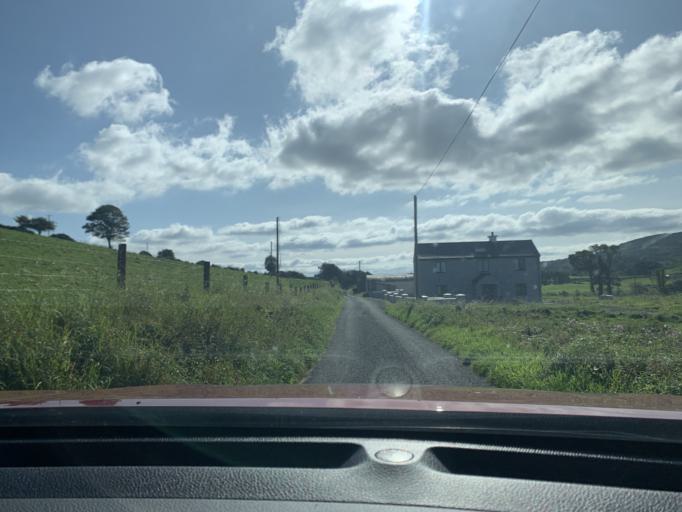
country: IE
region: Connaught
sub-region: Roscommon
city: Boyle
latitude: 54.0788
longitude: -8.3667
